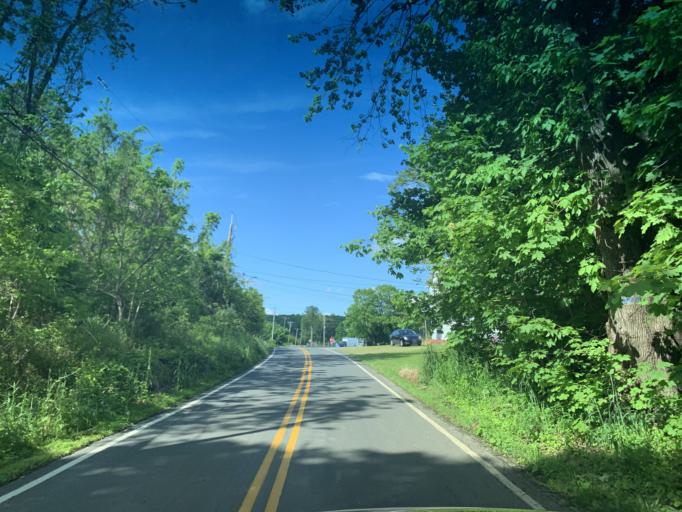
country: US
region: Maryland
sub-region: Cecil County
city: Rising Sun
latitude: 39.6981
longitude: -76.1805
